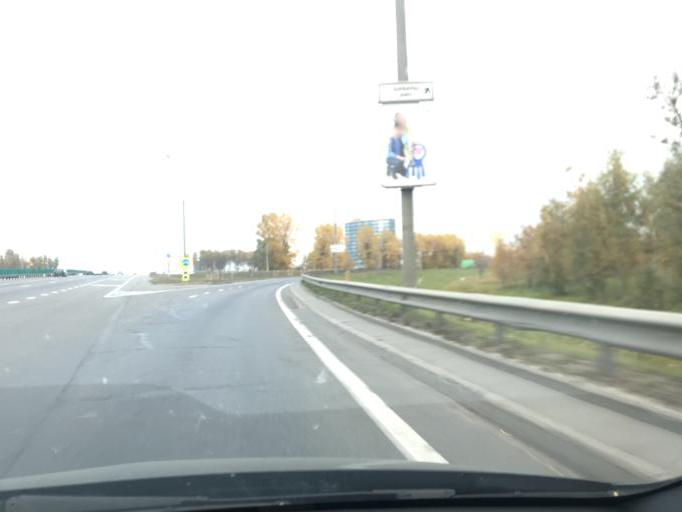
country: BY
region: Minsk
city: Vyaliki Trastsyanets
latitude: 53.8569
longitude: 27.6793
